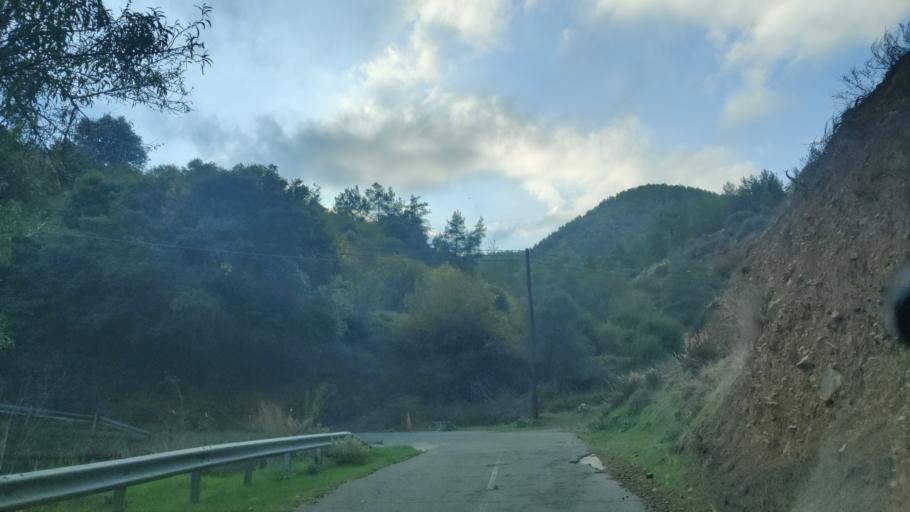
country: CY
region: Lefkosia
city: Lefka
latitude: 35.0594
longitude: 32.7349
